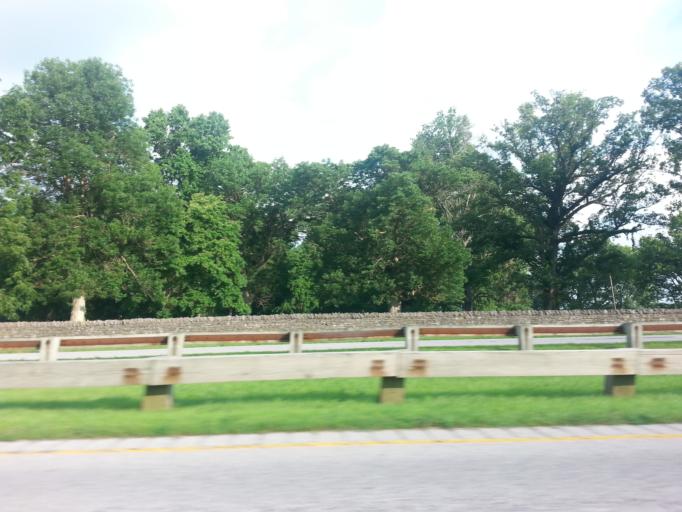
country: US
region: Kentucky
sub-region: Bourbon County
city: Paris
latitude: 38.1626
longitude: -84.3239
